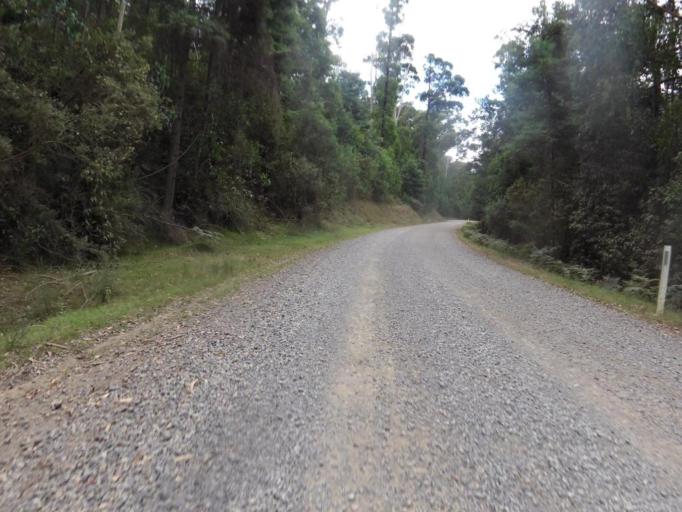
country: AU
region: Victoria
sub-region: Yarra Ranges
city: Healesville
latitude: -37.4084
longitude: 145.5592
